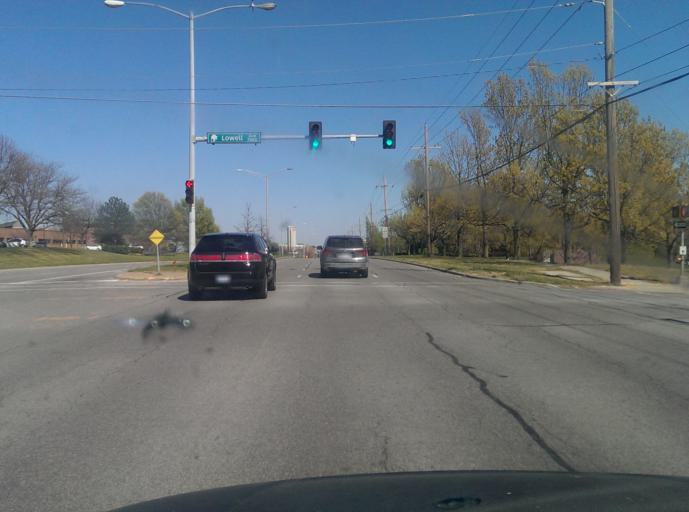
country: US
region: Kansas
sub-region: Johnson County
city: Overland Park
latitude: 38.9275
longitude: -94.6773
